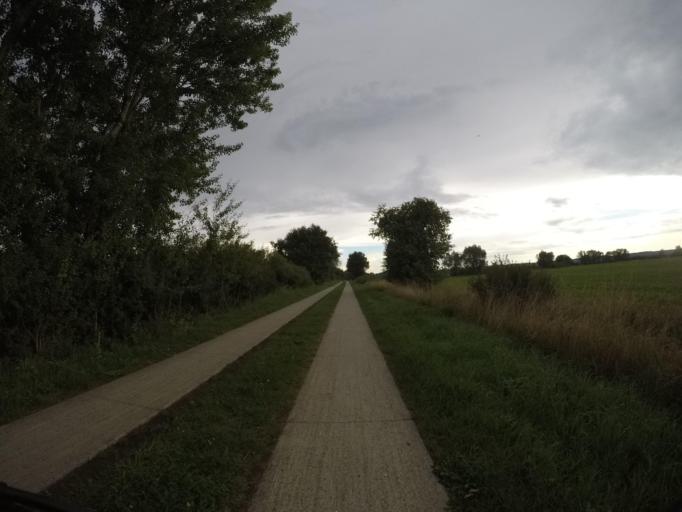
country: DE
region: Lower Saxony
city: Neu Darchau
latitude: 53.2609
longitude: 10.8798
